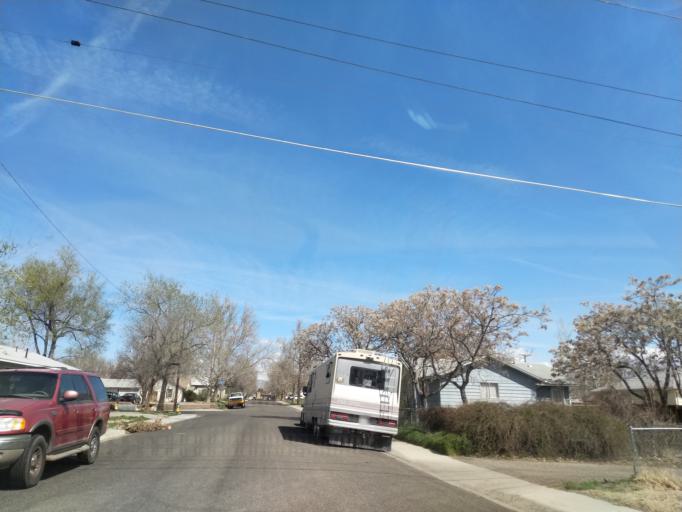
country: US
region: Colorado
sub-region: Mesa County
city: Grand Junction
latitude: 39.0804
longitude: -108.5454
